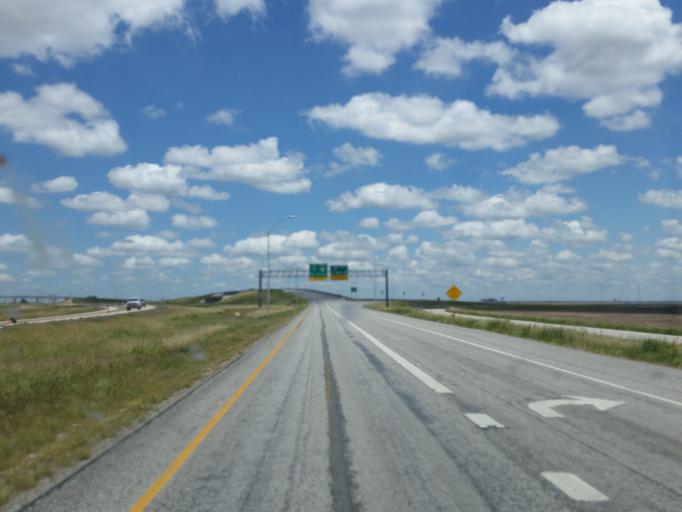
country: US
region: Texas
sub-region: Nolan County
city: Roscoe
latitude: 32.4465
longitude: -100.5112
